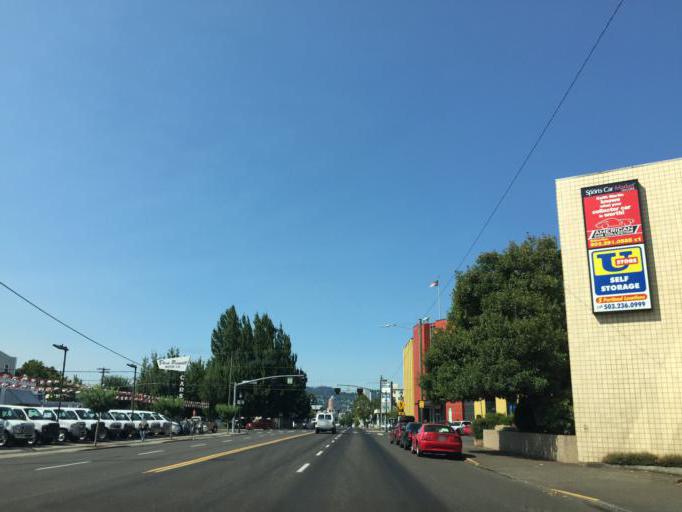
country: US
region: Oregon
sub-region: Multnomah County
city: Portland
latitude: 45.5256
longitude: -122.6464
